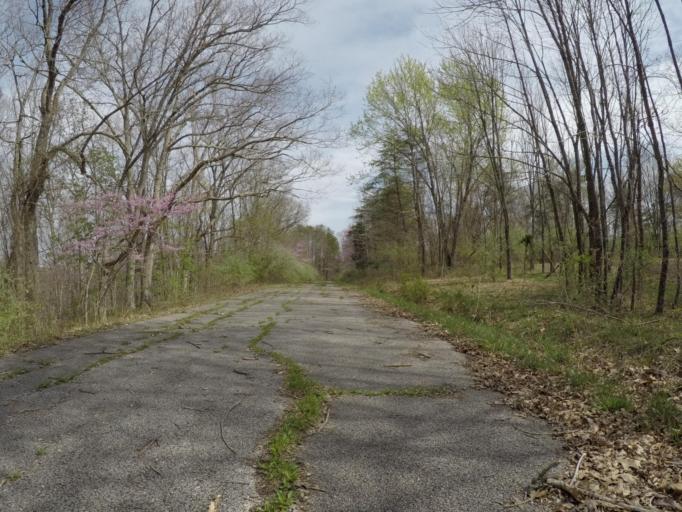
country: US
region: West Virginia
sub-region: Wayne County
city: Lavalette
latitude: 38.3193
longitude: -82.3514
